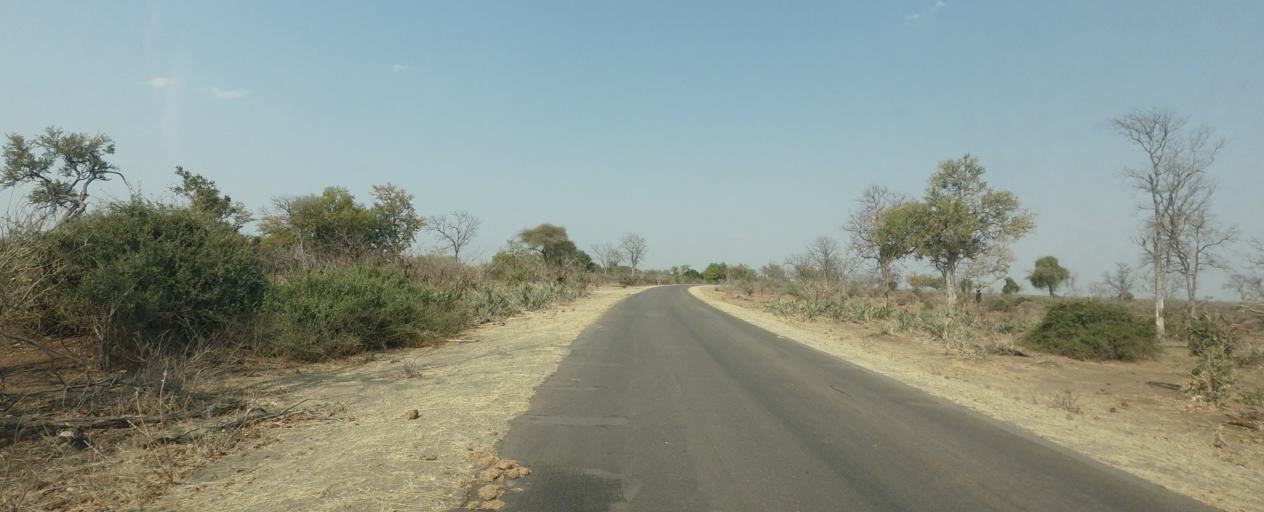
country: ZA
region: Limpopo
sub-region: Mopani District Municipality
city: Giyani
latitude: -23.0969
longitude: 31.3908
